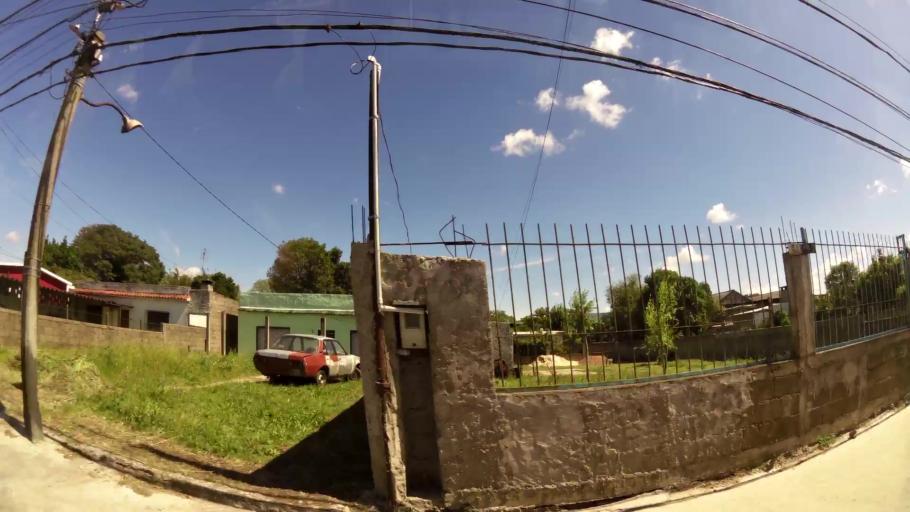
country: UY
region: Montevideo
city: Montevideo
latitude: -34.8474
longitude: -56.1311
